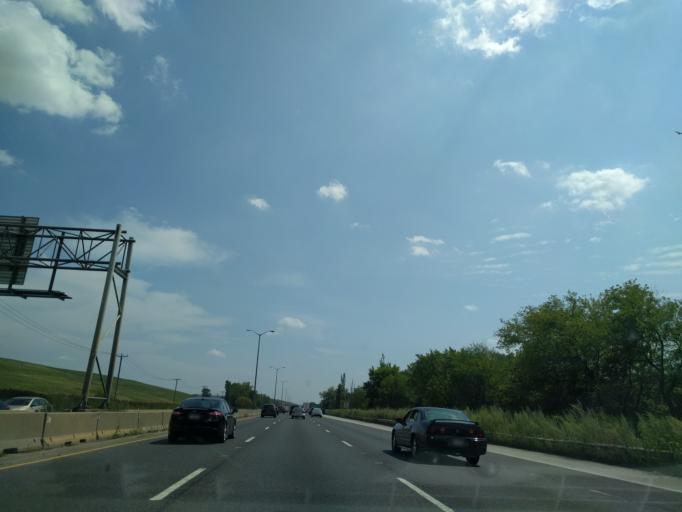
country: US
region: Illinois
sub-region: Cook County
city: Dolton
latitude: 41.6577
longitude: -87.5869
